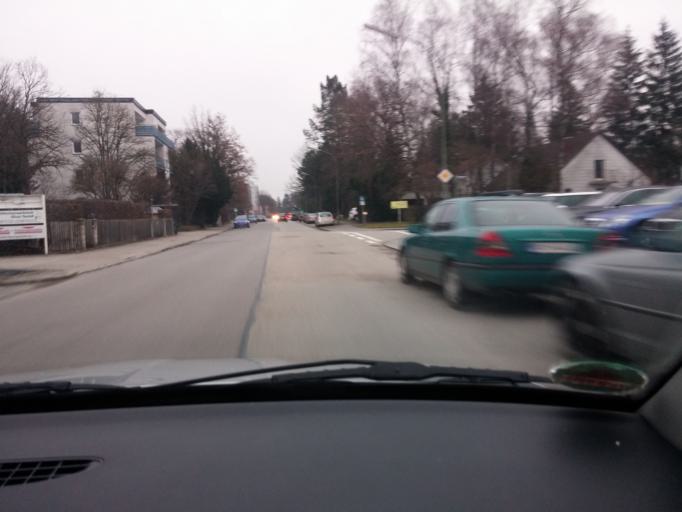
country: DE
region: Bavaria
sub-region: Upper Bavaria
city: Ottobrunn
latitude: 48.0685
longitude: 11.6736
